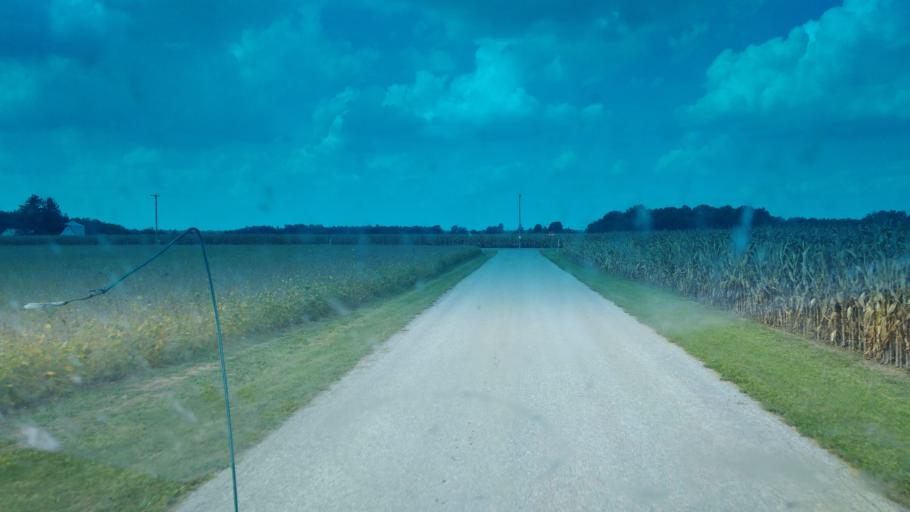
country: US
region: Ohio
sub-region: Hardin County
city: Kenton
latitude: 40.7304
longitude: -83.6144
